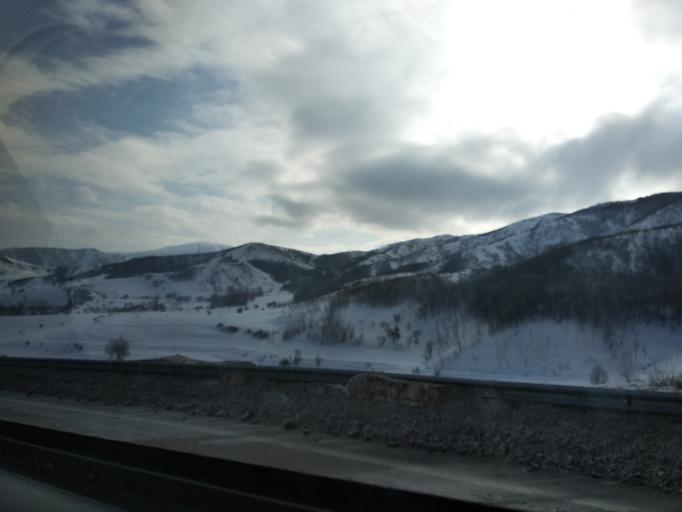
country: TR
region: Erzincan
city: Catalarmut
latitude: 39.8992
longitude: 39.3960
